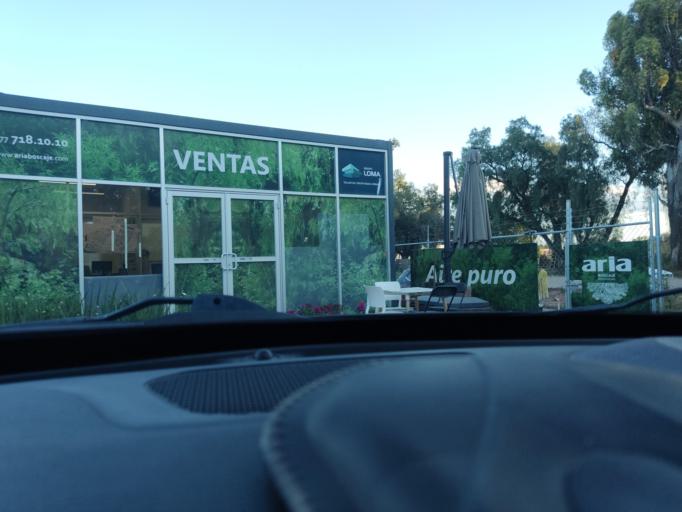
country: MX
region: Guanajuato
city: Leon
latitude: 21.1559
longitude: -101.6636
